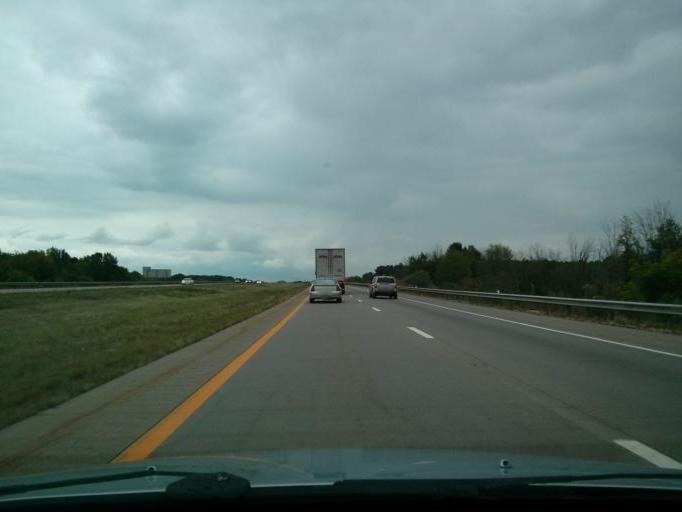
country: US
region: Ohio
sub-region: Trumbull County
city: Lordstown
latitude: 41.1069
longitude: -80.8730
